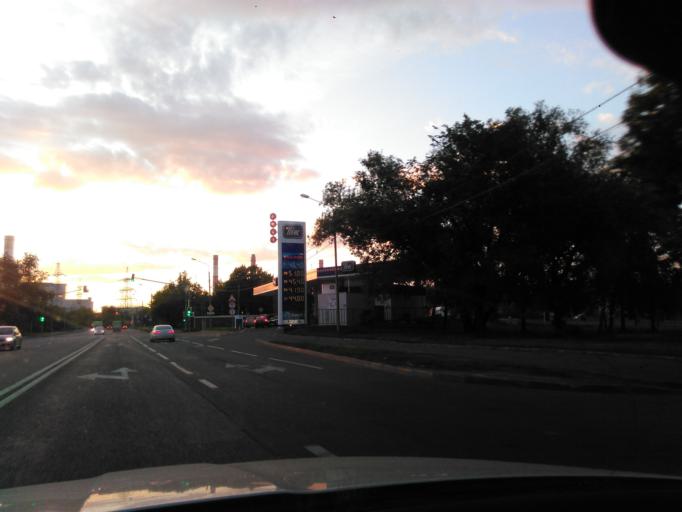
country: RU
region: Moscow
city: Businovo
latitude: 55.8866
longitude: 37.5145
